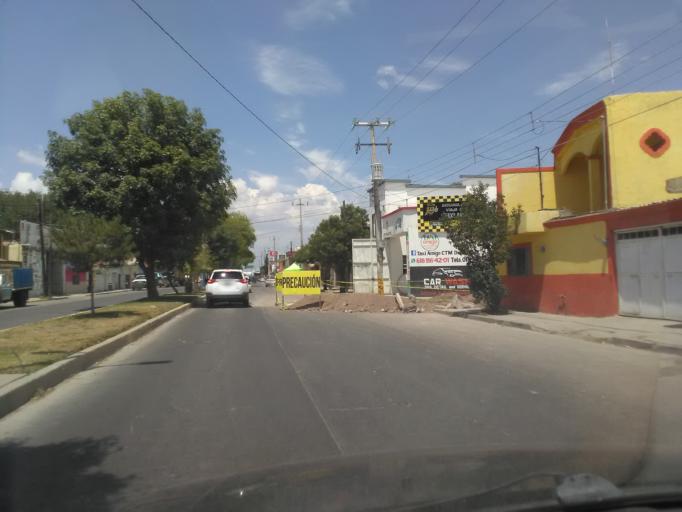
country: MX
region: Durango
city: Victoria de Durango
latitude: 24.0202
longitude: -104.6288
